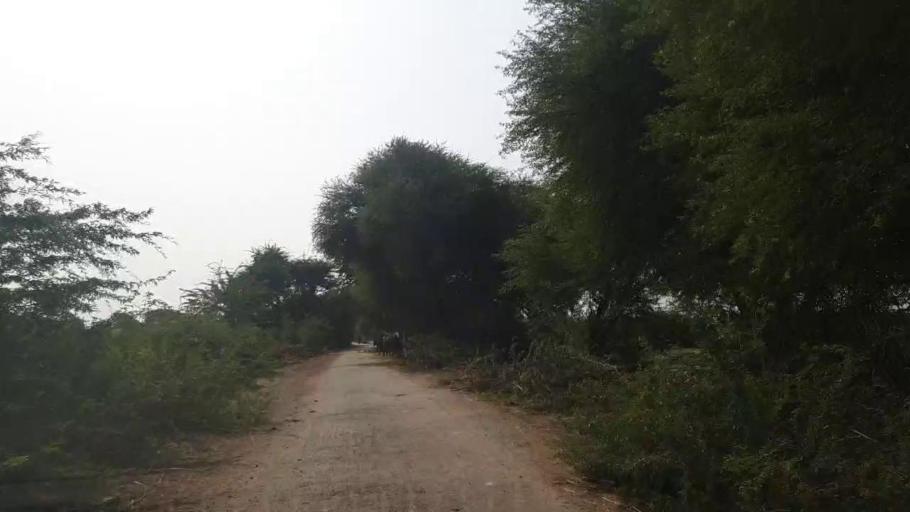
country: PK
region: Sindh
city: Badin
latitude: 24.7376
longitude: 68.7355
